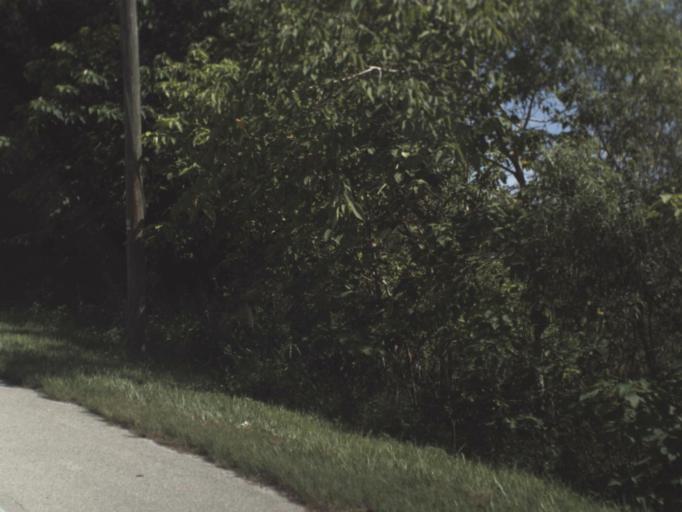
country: US
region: Florida
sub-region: Polk County
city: Polk City
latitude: 28.1359
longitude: -81.7950
